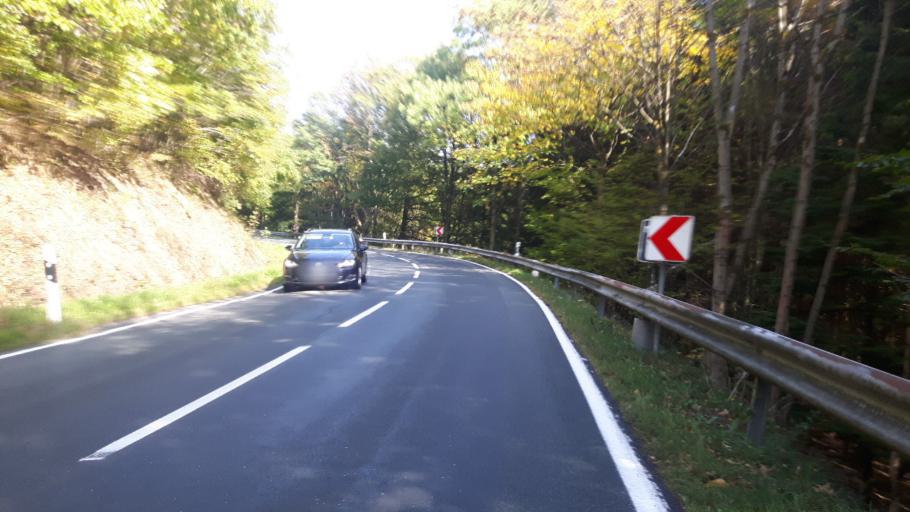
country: DE
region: North Rhine-Westphalia
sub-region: Regierungsbezirk Arnsberg
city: Erndtebruck
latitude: 50.9154
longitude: 8.2218
